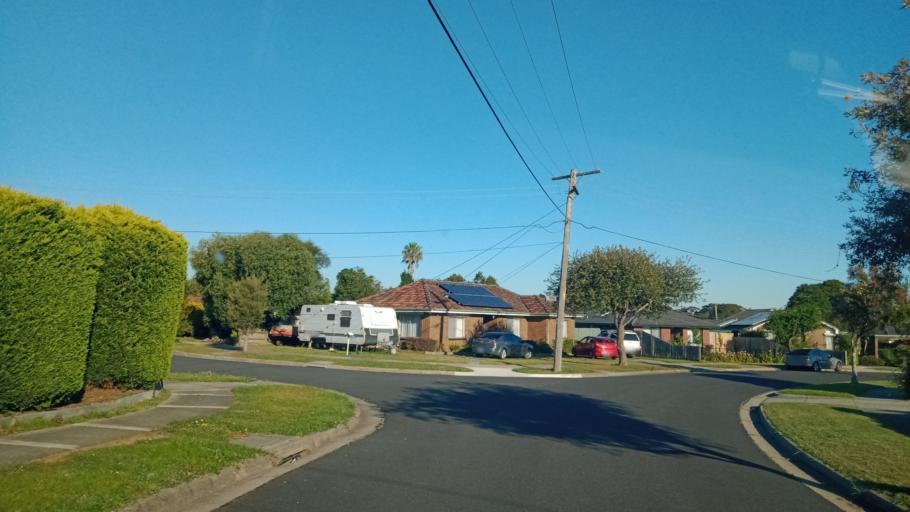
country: AU
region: Victoria
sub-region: Greater Dandenong
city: Noble Park North
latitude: -37.9319
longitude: 145.1741
